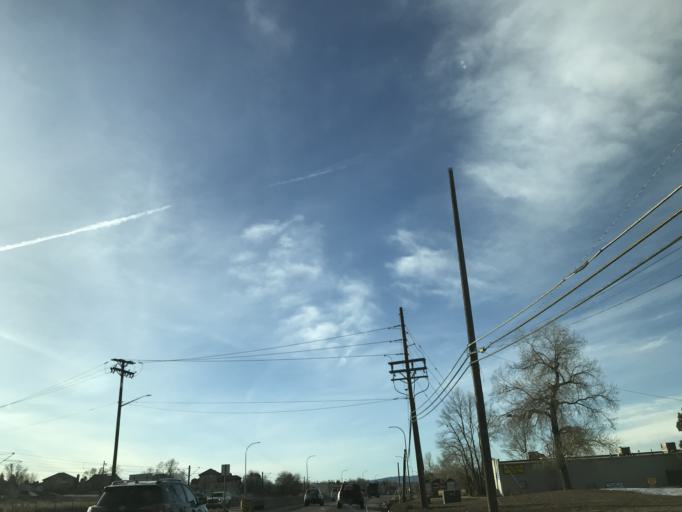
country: US
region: Colorado
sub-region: Arapahoe County
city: Littleton
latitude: 39.6030
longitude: -105.0204
